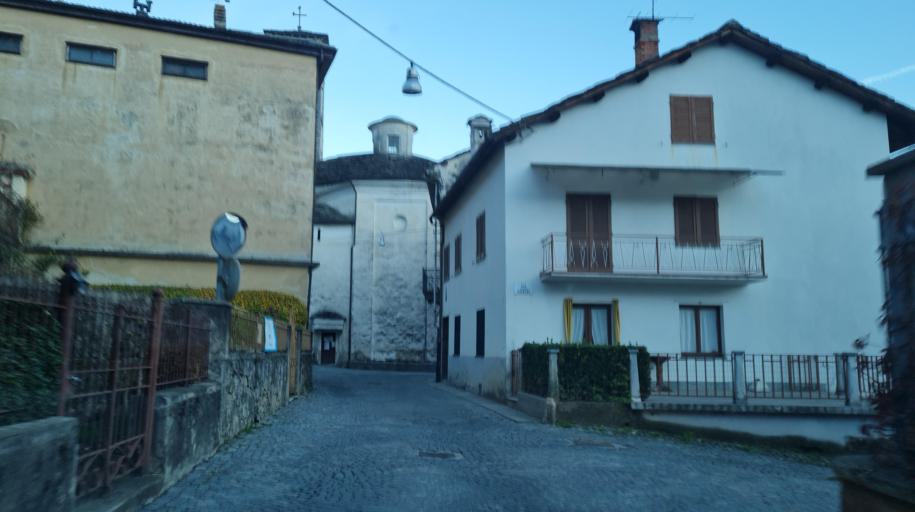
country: IT
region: Piedmont
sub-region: Provincia di Torino
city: Trausella
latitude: 45.4979
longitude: 7.7660
